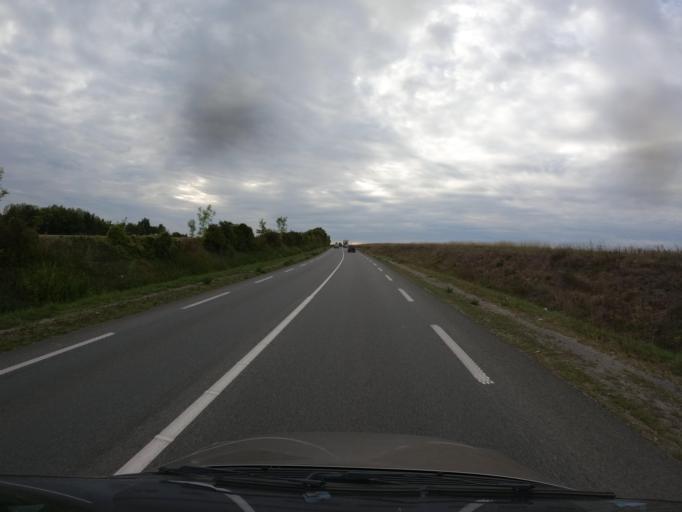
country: FR
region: Poitou-Charentes
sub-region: Departement de la Vienne
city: Migne-Auxances
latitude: 46.6336
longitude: 0.2885
